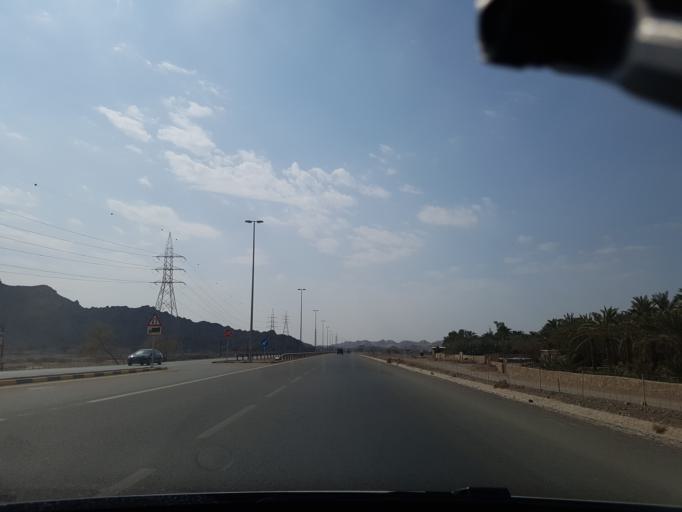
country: AE
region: Al Fujayrah
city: Dibba Al-Fujairah
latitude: 25.4917
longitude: 56.0482
